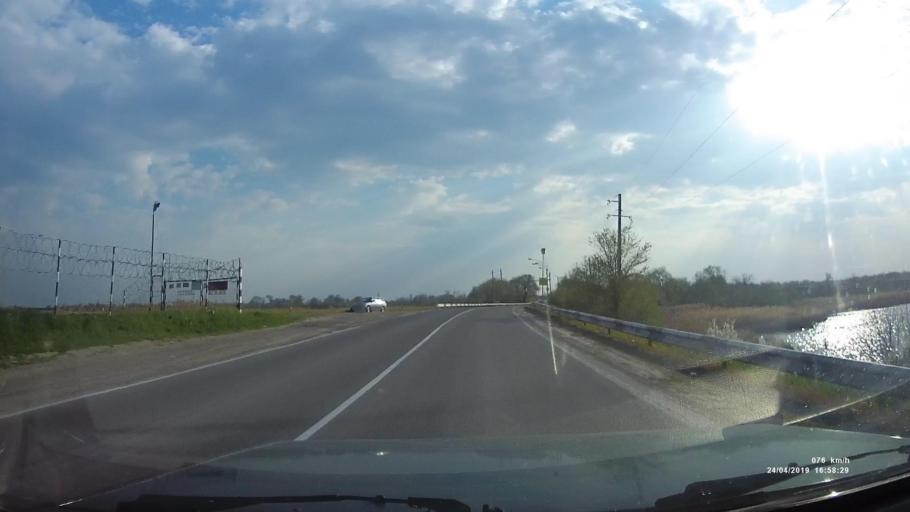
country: RU
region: Rostov
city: Proletarsk
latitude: 46.6274
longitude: 41.6584
